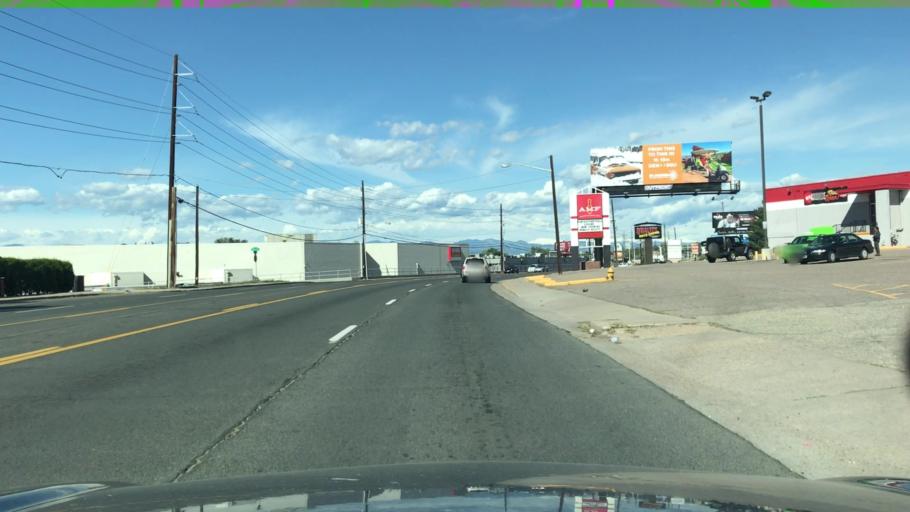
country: US
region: Colorado
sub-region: Arapahoe County
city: Glendale
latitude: 39.7007
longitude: -104.9094
